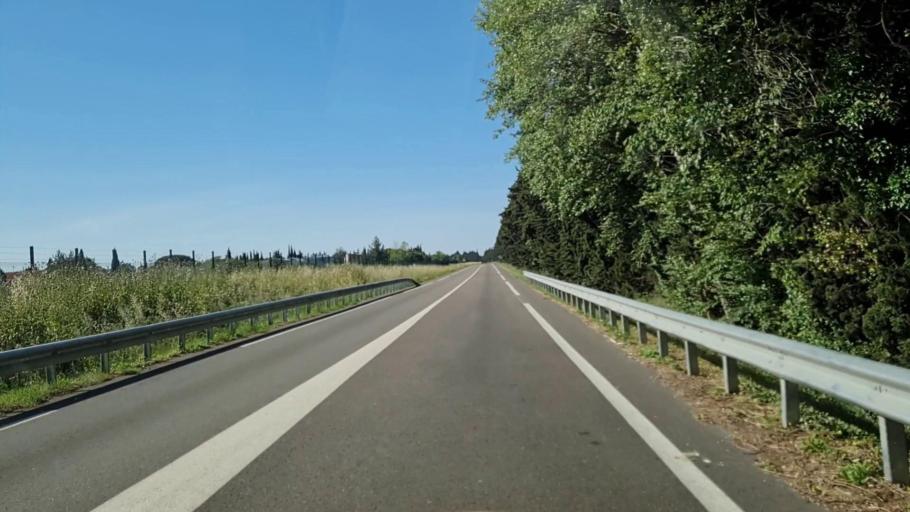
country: FR
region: Languedoc-Roussillon
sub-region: Departement du Gard
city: Garons
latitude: 43.7592
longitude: 4.4060
